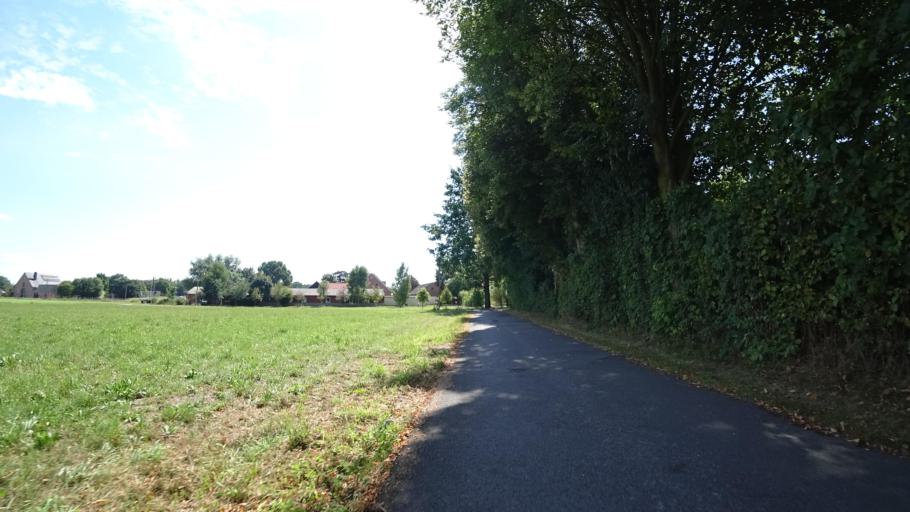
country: DE
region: North Rhine-Westphalia
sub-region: Regierungsbezirk Detmold
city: Guetersloh
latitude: 51.9510
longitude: 8.3886
